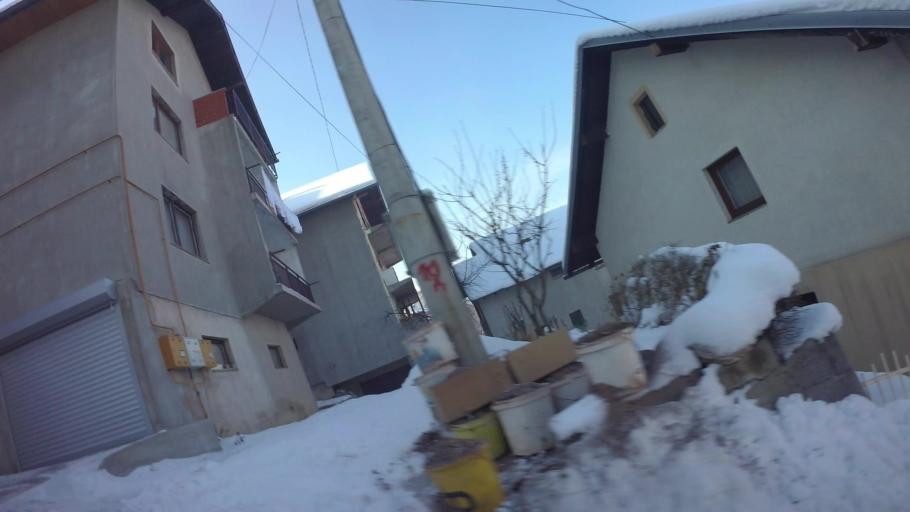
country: BA
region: Federation of Bosnia and Herzegovina
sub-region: Kanton Sarajevo
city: Sarajevo
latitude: 43.8399
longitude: 18.3636
